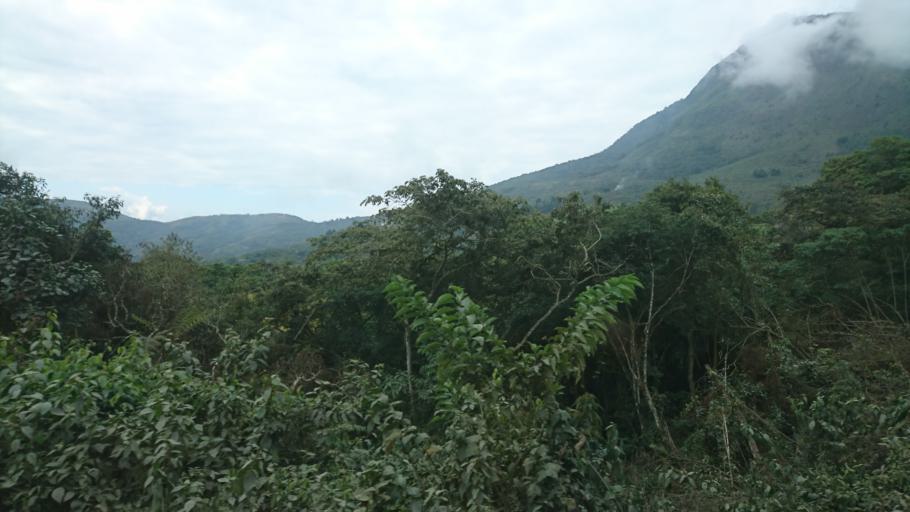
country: BO
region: La Paz
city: Coroico
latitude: -16.2283
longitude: -67.6793
